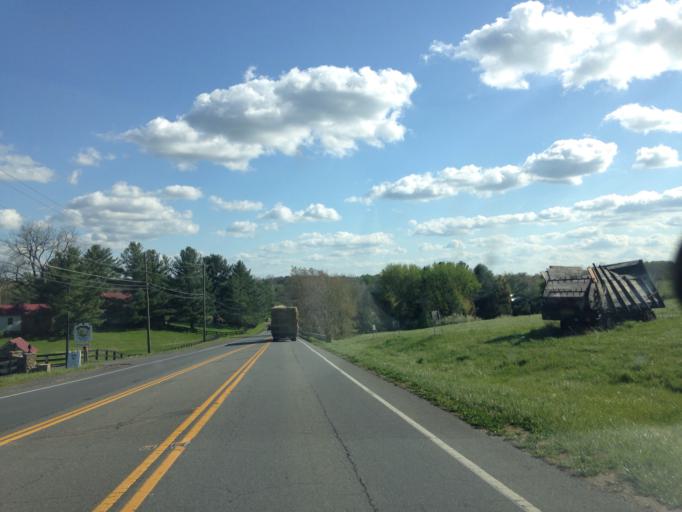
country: US
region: Virginia
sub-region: Loudoun County
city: Purcellville
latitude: 39.1973
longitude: -77.6737
